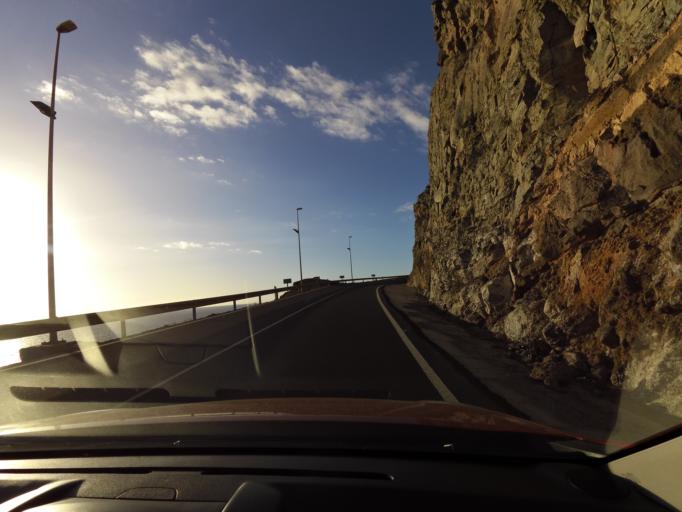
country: ES
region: Canary Islands
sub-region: Provincia de Las Palmas
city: Puerto Rico
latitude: 27.7874
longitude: -15.7220
